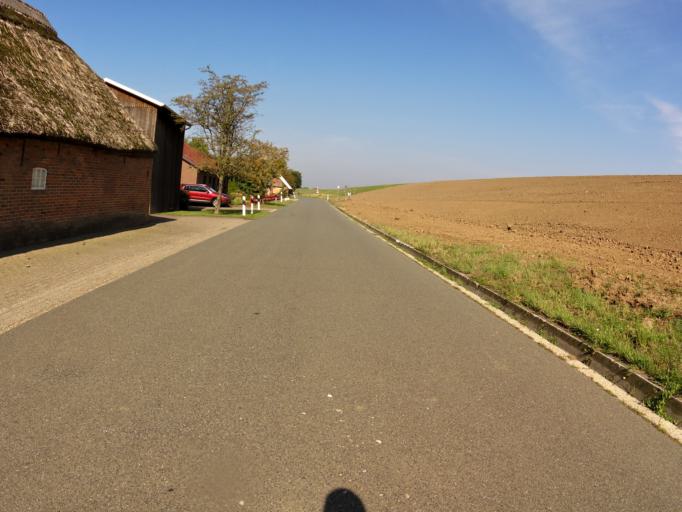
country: DE
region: Lower Saxony
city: Neuenkirchen
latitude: 53.2027
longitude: 8.4936
